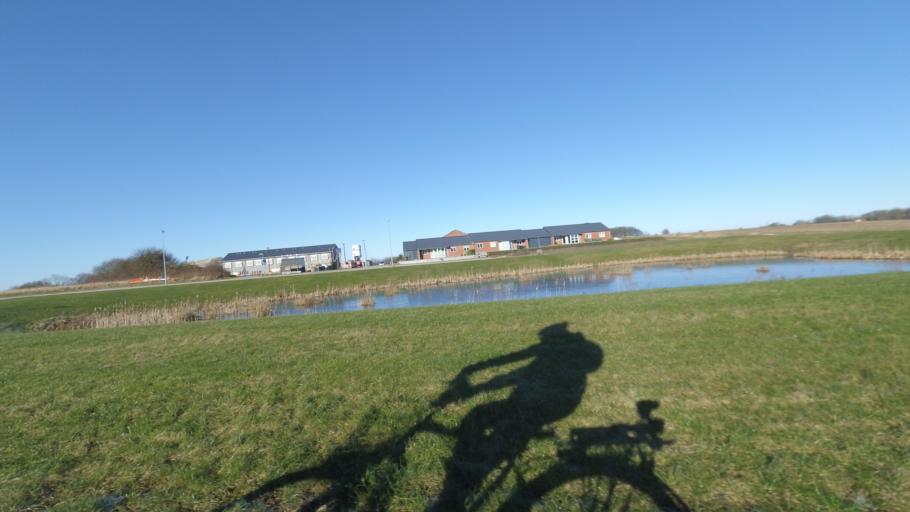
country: DK
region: Central Jutland
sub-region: Arhus Kommune
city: Kolt
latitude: 56.1142
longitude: 10.0922
